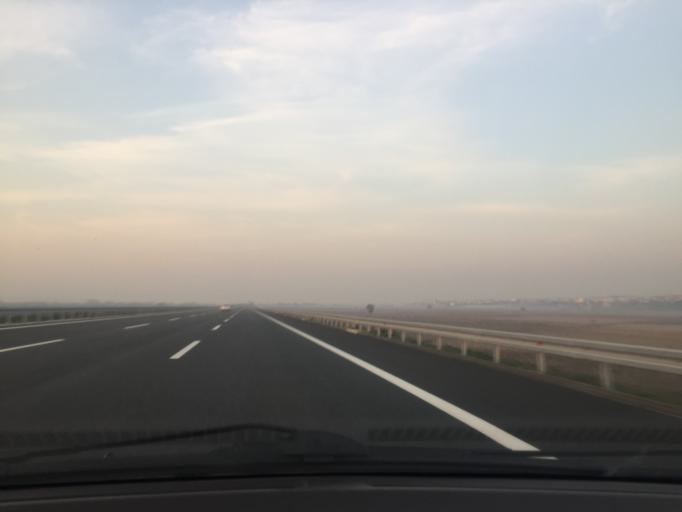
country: TR
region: Bursa
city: Karacabey
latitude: 40.2159
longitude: 28.3936
